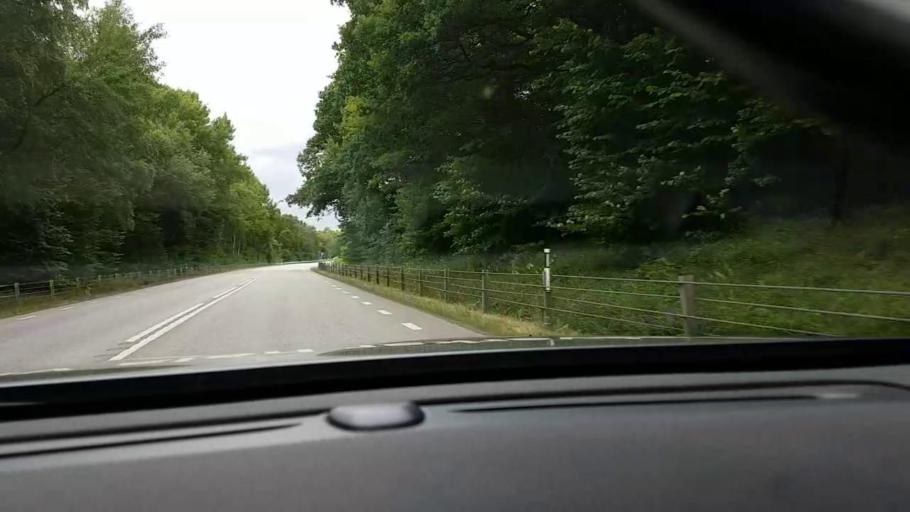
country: SE
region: Skane
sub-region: Horby Kommun
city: Hoerby
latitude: 55.8713
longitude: 13.6350
